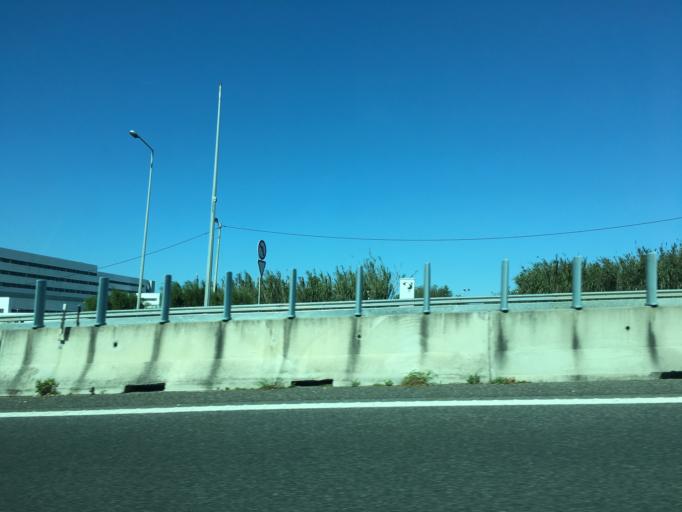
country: PT
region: Lisbon
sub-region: Cascais
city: Alcabideche
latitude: 38.7312
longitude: -9.4158
